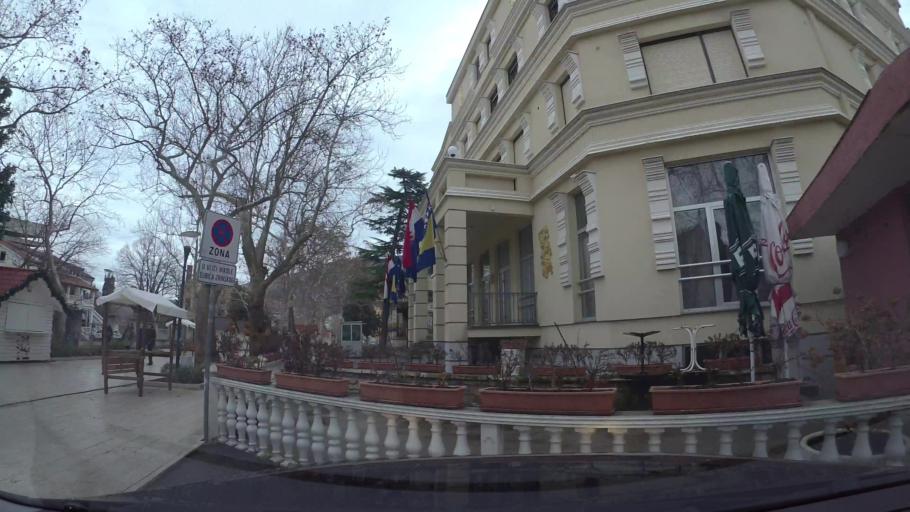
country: BA
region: Federation of Bosnia and Herzegovina
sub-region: Hercegovacko-Bosanski Kanton
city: Mostar
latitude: 43.3425
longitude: 17.8055
